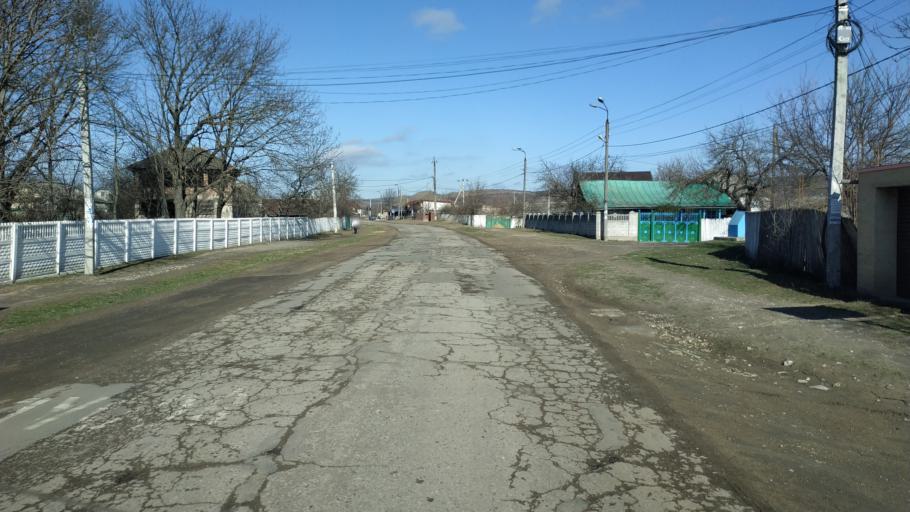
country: MD
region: Hincesti
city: Hincesti
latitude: 46.9611
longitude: 28.6029
